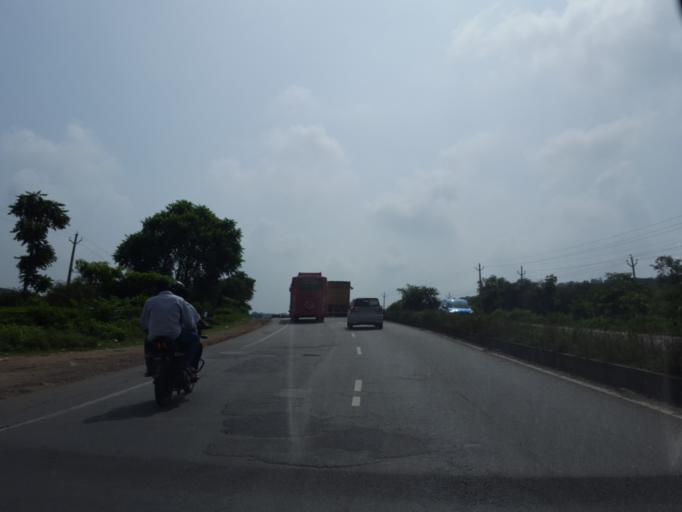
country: IN
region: Telangana
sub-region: Rangareddi
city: Ghatkesar
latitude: 17.2856
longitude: 78.7749
